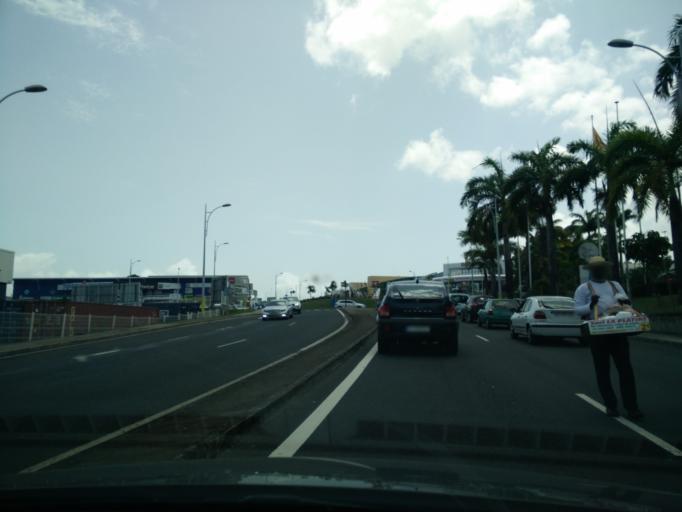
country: GP
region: Guadeloupe
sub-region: Guadeloupe
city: Baie-Mahault
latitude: 16.2408
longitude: -61.5818
